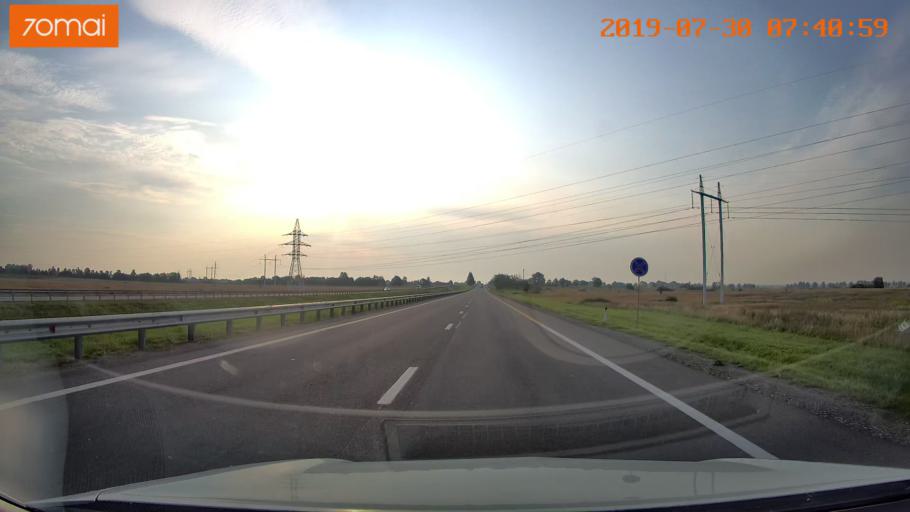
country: RU
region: Kaliningrad
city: Gvardeysk
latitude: 54.6484
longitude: 21.2377
